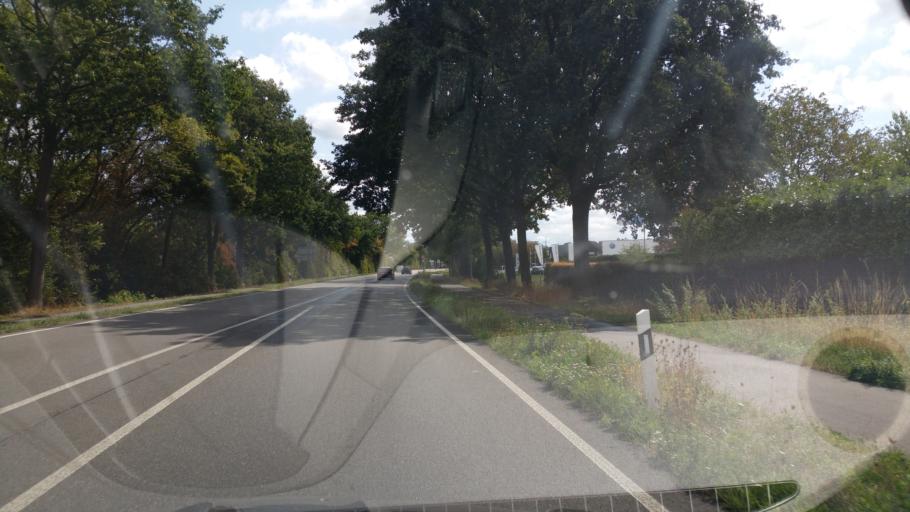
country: DE
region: North Rhine-Westphalia
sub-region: Regierungsbezirk Dusseldorf
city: Hamminkeln
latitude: 51.7369
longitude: 6.5990
